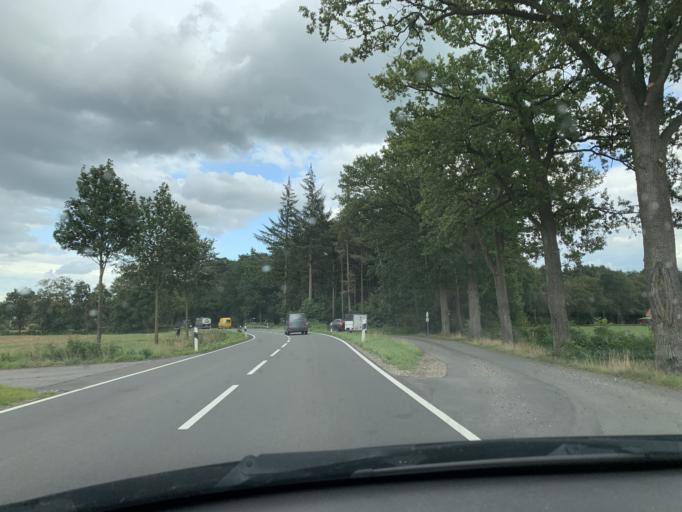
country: DE
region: Lower Saxony
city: Westerstede
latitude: 53.2854
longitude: 7.9911
